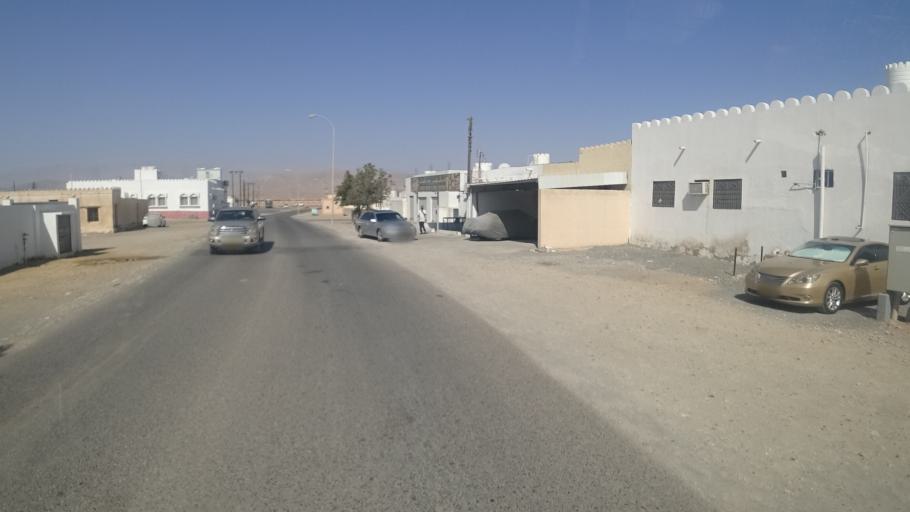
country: OM
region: Ash Sharqiyah
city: Sur
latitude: 22.5406
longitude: 59.4849
